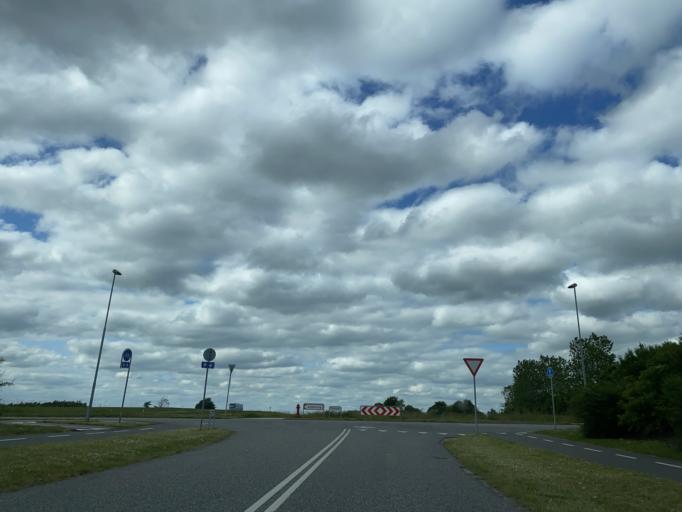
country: DK
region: Central Jutland
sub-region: Arhus Kommune
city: Framlev
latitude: 56.1477
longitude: 9.9868
